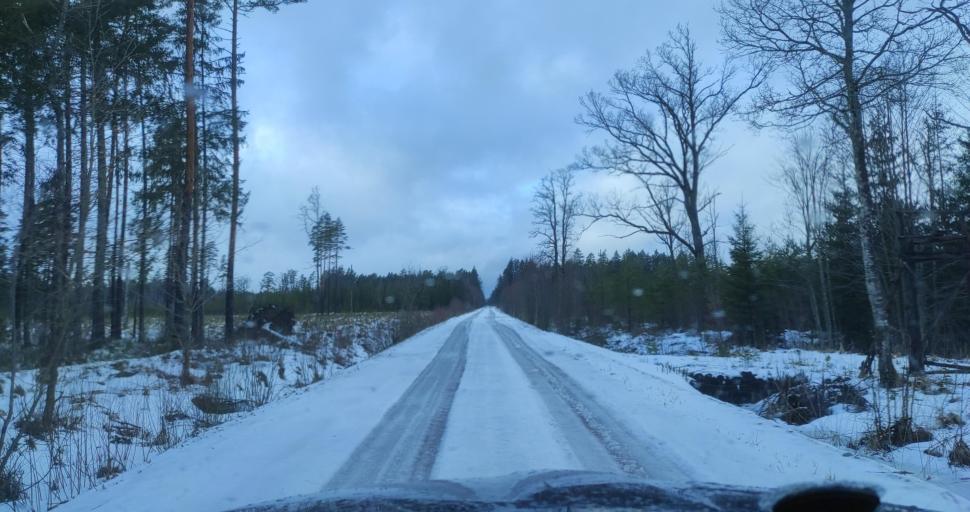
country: LV
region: Dundaga
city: Dundaga
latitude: 57.4086
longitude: 22.0874
